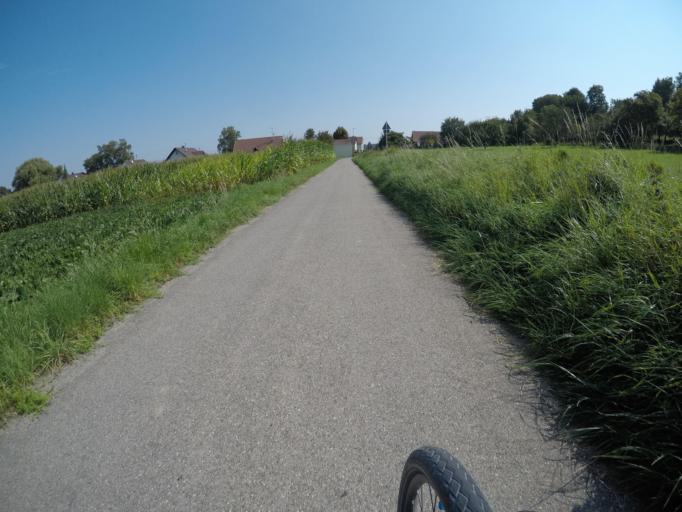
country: DE
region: Bavaria
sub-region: Swabia
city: Holzheim
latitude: 48.5123
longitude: 10.5064
